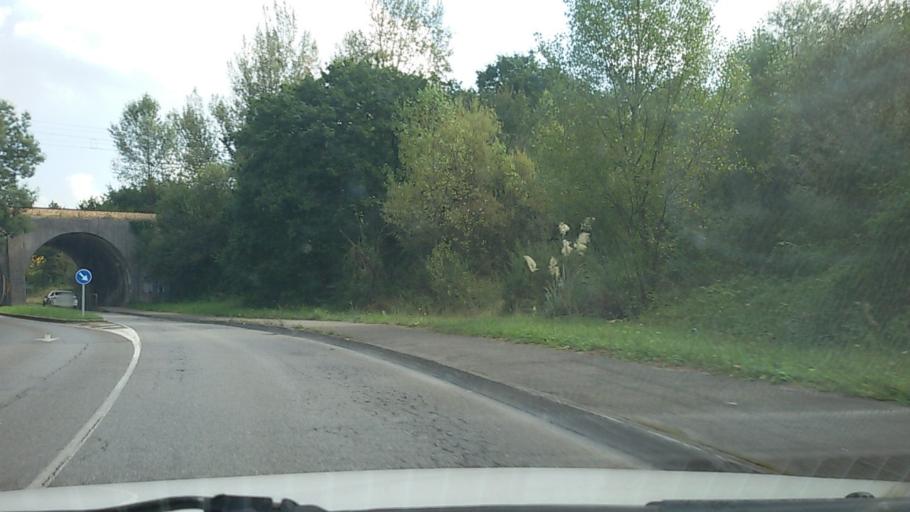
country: ES
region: Asturias
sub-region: Province of Asturias
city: Lugones
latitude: 43.4103
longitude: -5.7943
